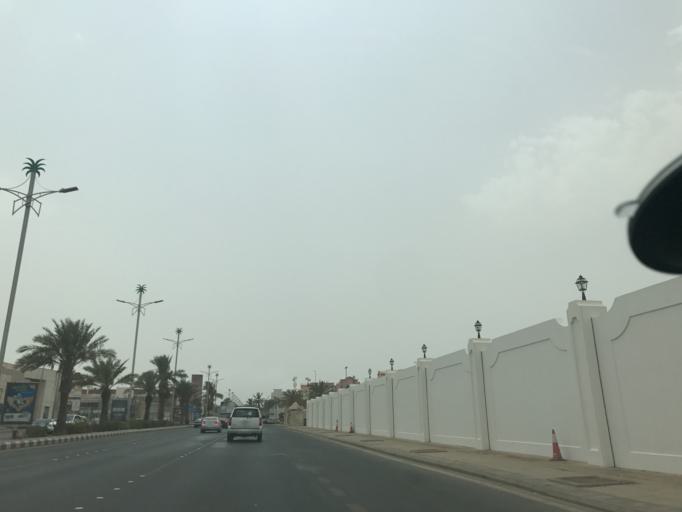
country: SA
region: Makkah
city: Jeddah
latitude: 21.5496
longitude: 39.1511
